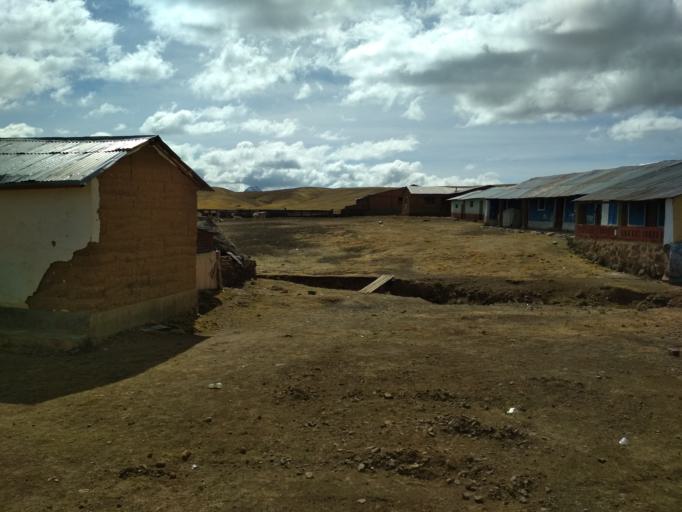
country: PE
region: Huancavelica
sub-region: Provincia de Huancavelica
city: Acobambilla
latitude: -12.7261
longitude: -75.5070
